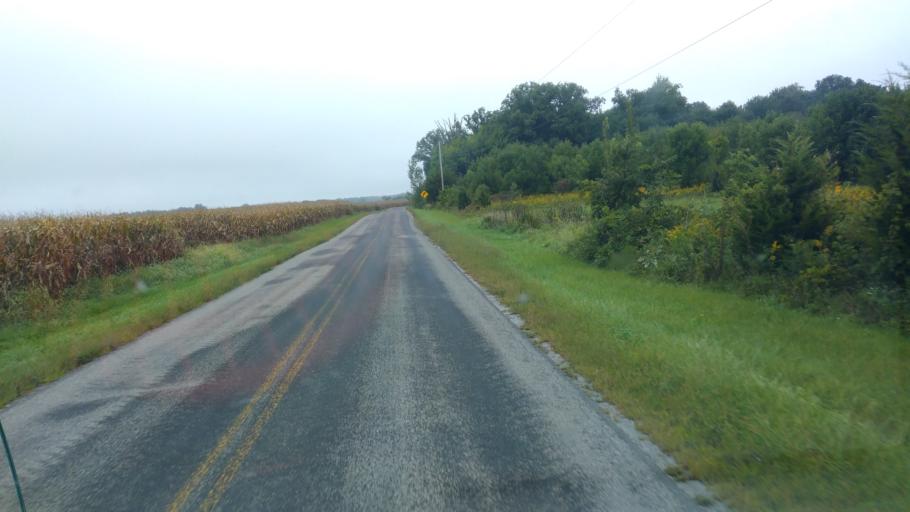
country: US
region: Ohio
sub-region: Logan County
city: Northwood
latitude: 40.5287
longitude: -83.6280
